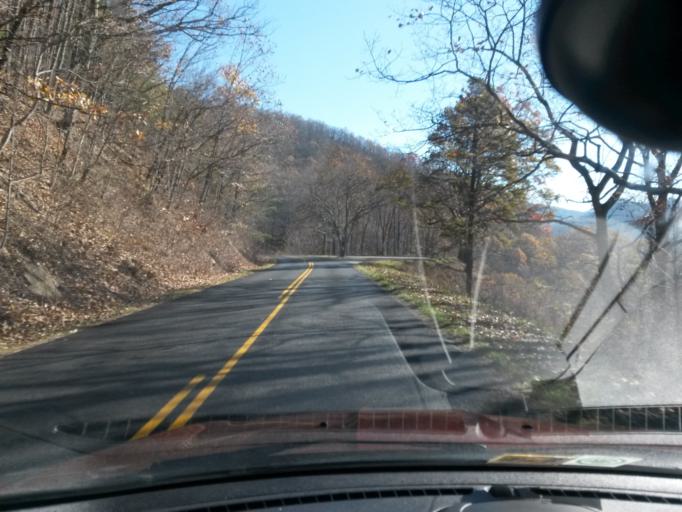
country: US
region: Virginia
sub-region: Botetourt County
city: Buchanan
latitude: 37.4800
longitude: -79.6559
